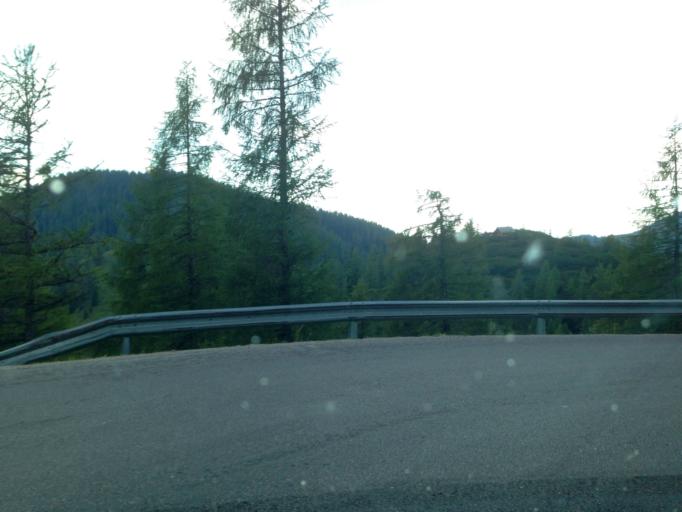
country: AT
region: Salzburg
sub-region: Politischer Bezirk Sankt Johann im Pongau
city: Filzmoos
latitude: 47.4471
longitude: 13.6088
